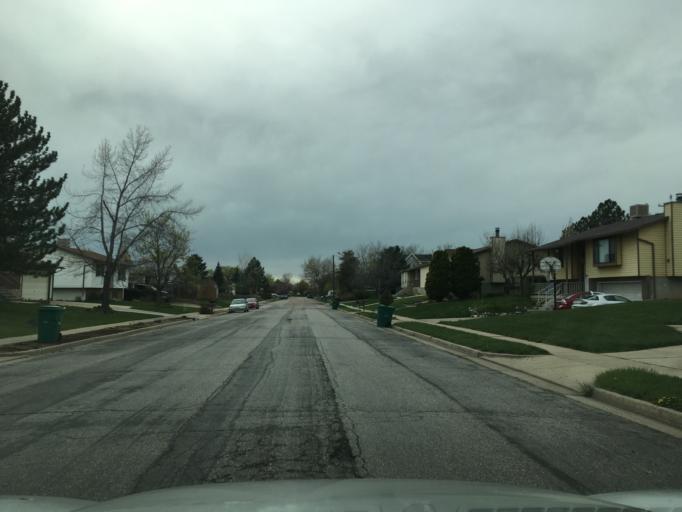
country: US
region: Utah
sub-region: Davis County
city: Layton
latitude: 41.0779
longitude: -111.9910
